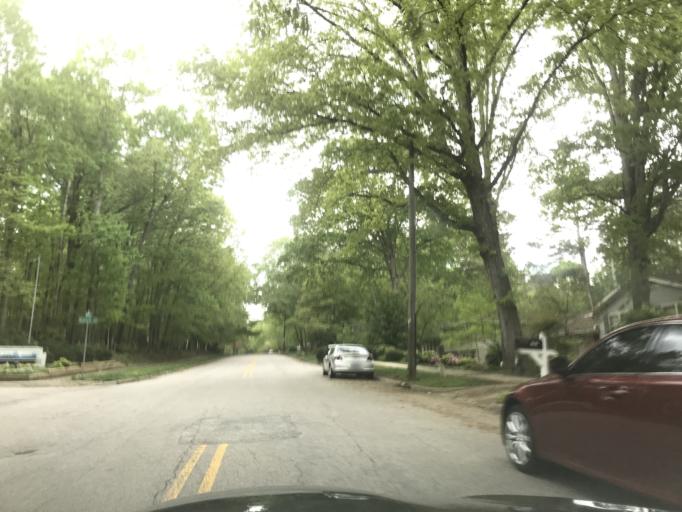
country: US
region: North Carolina
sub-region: Wake County
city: West Raleigh
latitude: 35.7827
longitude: -78.7070
